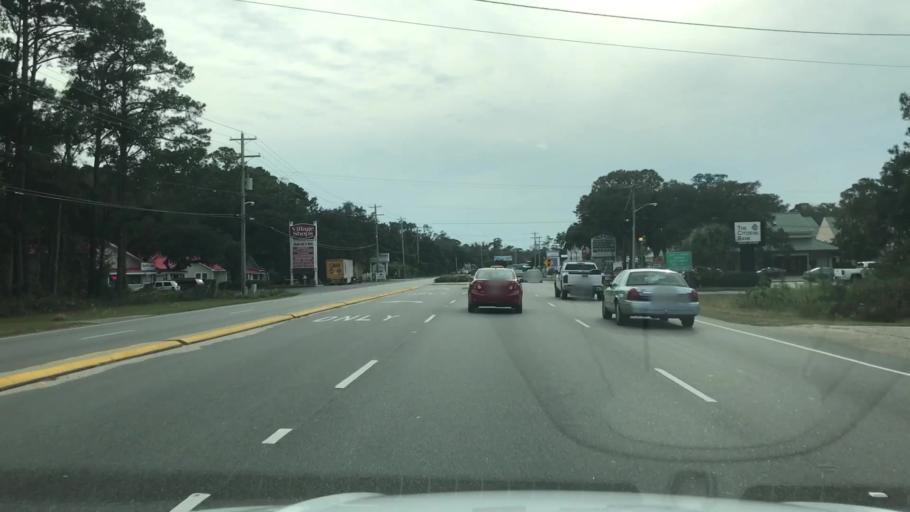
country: US
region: South Carolina
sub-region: Georgetown County
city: Murrells Inlet
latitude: 33.4426
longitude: -79.1244
